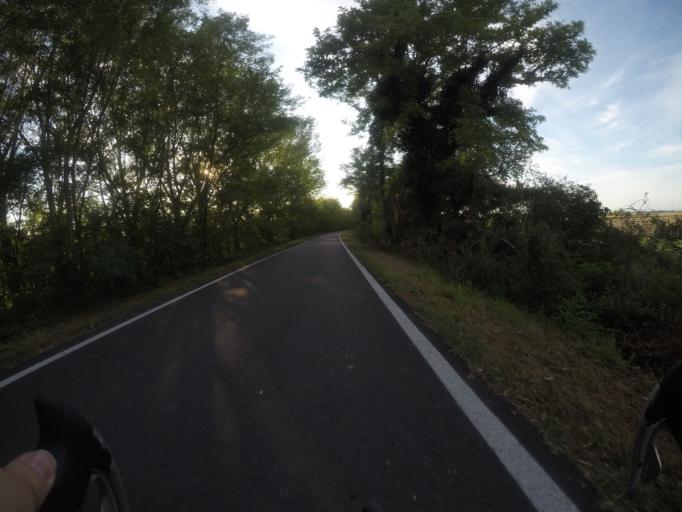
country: IT
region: Veneto
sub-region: Provincia di Rovigo
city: Pincara
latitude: 44.9961
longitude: 11.5900
